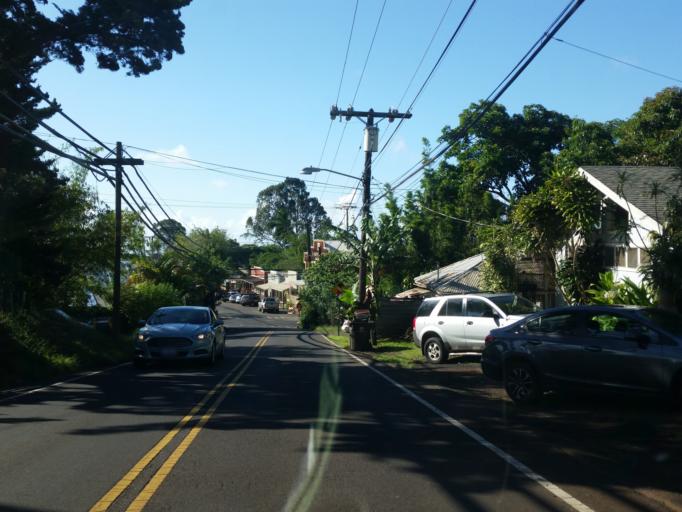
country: US
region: Hawaii
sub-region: Maui County
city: Makawao
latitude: 20.8533
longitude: -156.3100
